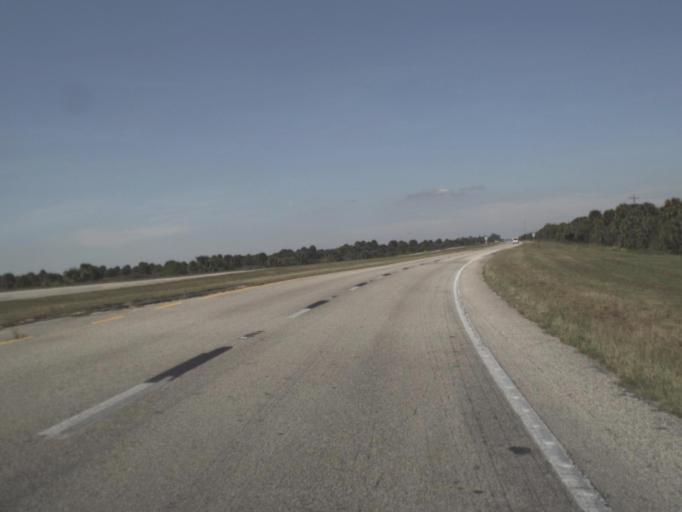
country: US
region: Florida
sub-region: Glades County
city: Moore Haven
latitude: 26.8354
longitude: -81.1917
